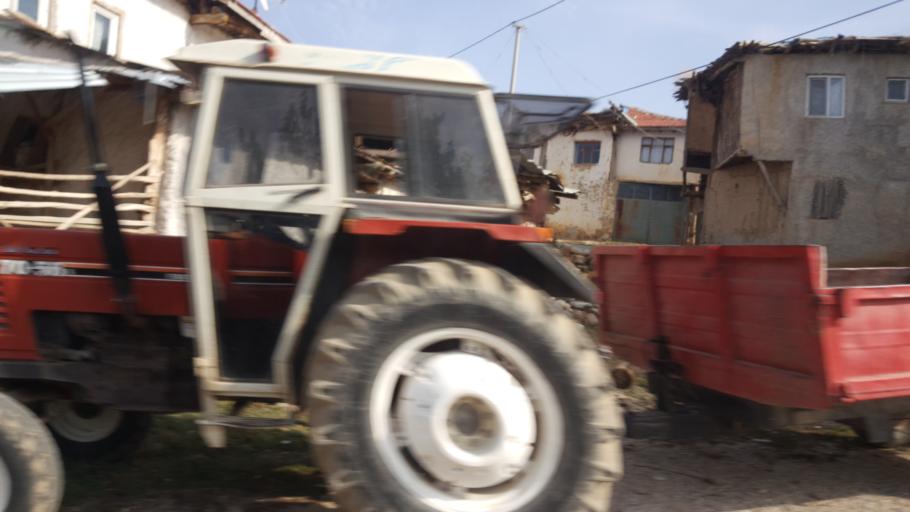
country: TR
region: Eskisehir
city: Mihaliccik
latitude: 39.9782
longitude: 31.3716
